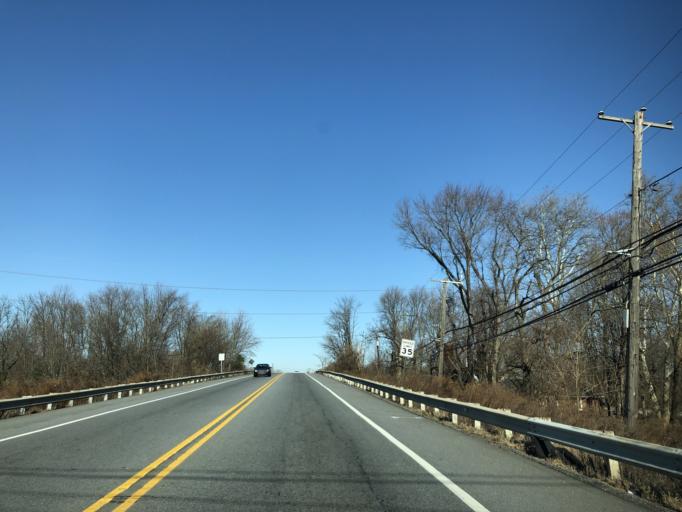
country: US
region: Pennsylvania
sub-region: Delaware County
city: Linwood
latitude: 39.8393
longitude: -75.4249
